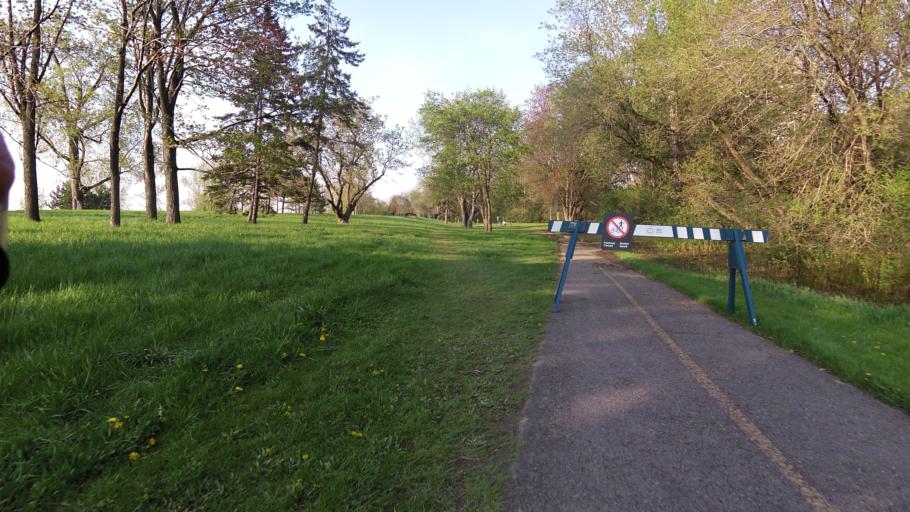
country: CA
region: Ontario
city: Bells Corners
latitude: 45.3750
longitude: -75.7814
